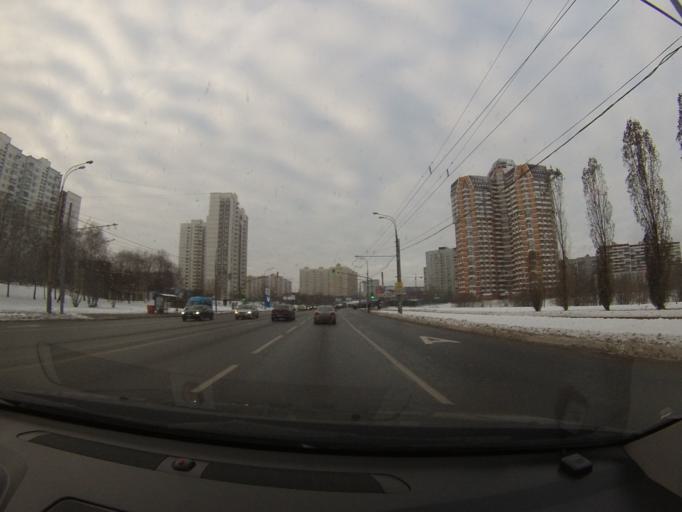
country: RU
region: Moscow
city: Nikulino
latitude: 55.6738
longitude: 37.4588
